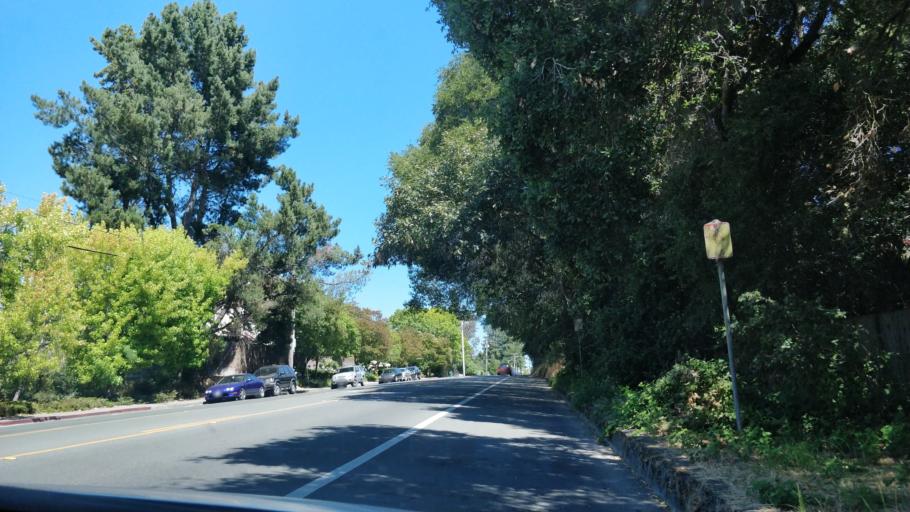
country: US
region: California
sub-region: Sonoma County
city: Sebastopol
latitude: 38.3980
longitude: -122.8423
